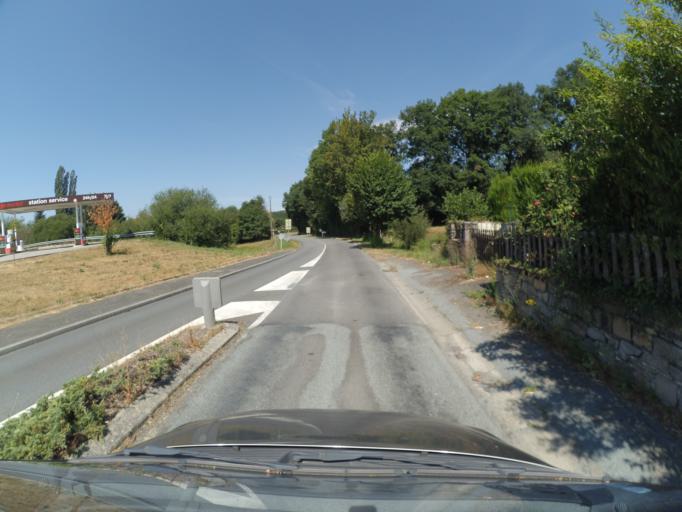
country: FR
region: Limousin
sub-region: Departement de la Creuse
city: Bourganeuf
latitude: 45.9594
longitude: 1.7603
